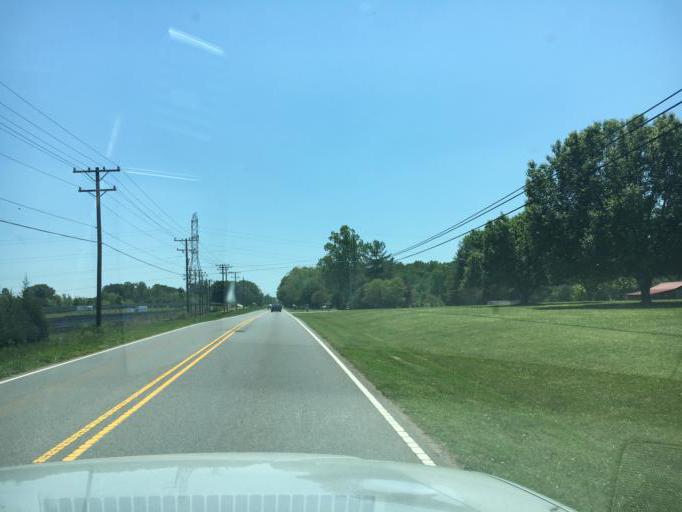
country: US
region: North Carolina
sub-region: Cleveland County
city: Shelby
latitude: 35.2347
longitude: -81.5662
